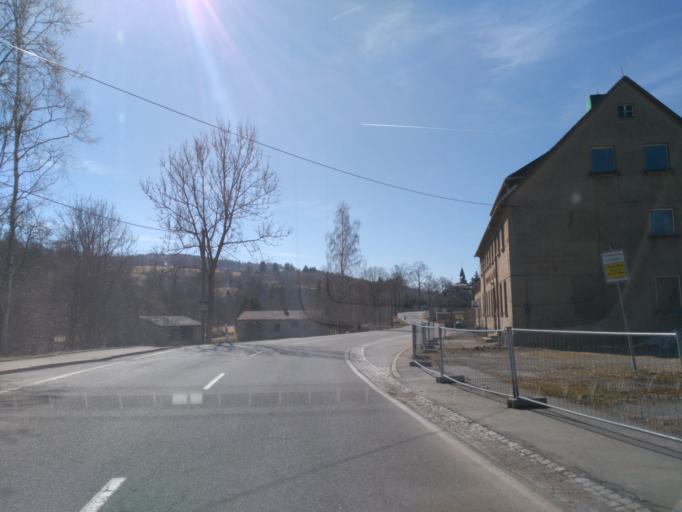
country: CZ
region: Ustecky
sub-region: Okres Chomutov
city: Vejprty
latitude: 50.4747
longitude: 13.0187
